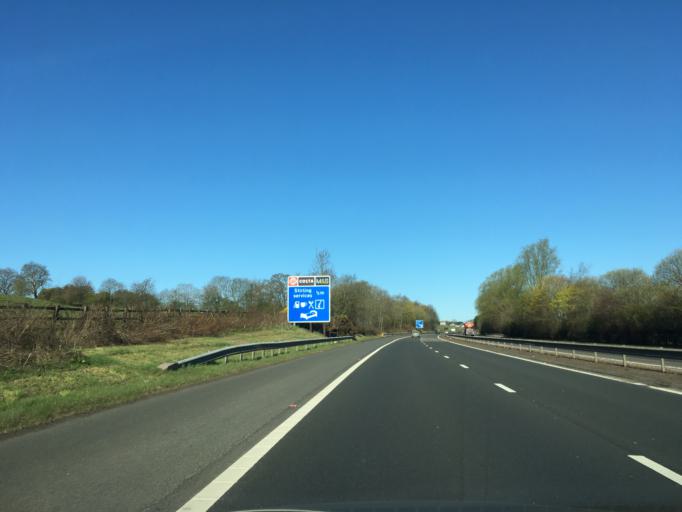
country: GB
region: Scotland
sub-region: Stirling
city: Plean
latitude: 56.0691
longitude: -3.8936
